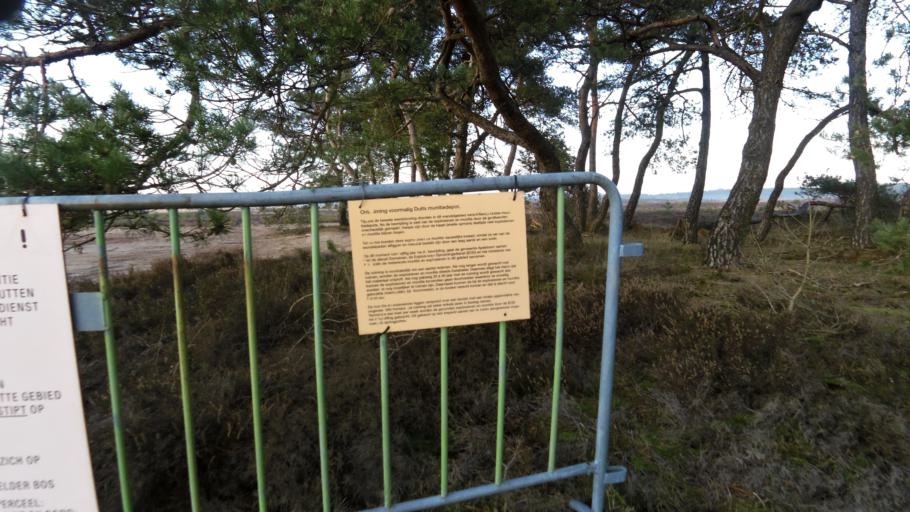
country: NL
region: Gelderland
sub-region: Gemeente Apeldoorn
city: Uddel
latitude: 52.2323
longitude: 5.8001
